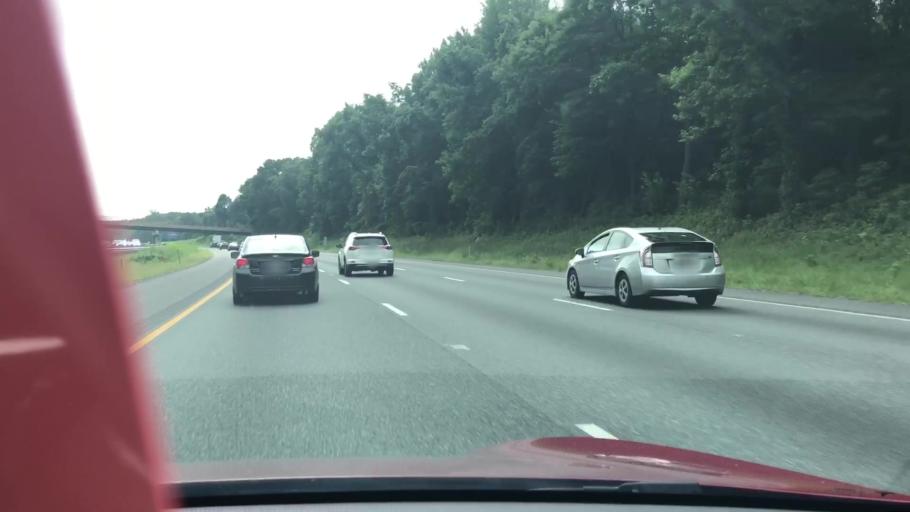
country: US
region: Maryland
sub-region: Harford County
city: Havre de Grace
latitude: 39.5736
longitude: -76.1364
